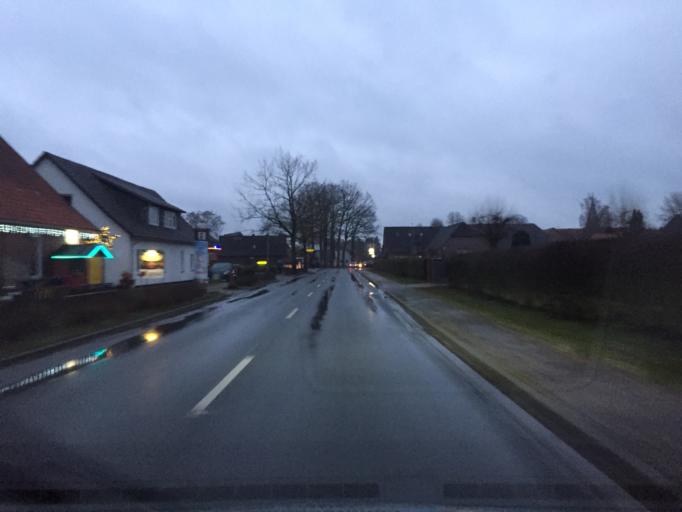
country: DE
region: Lower Saxony
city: Sudwalde
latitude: 52.7978
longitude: 8.8426
